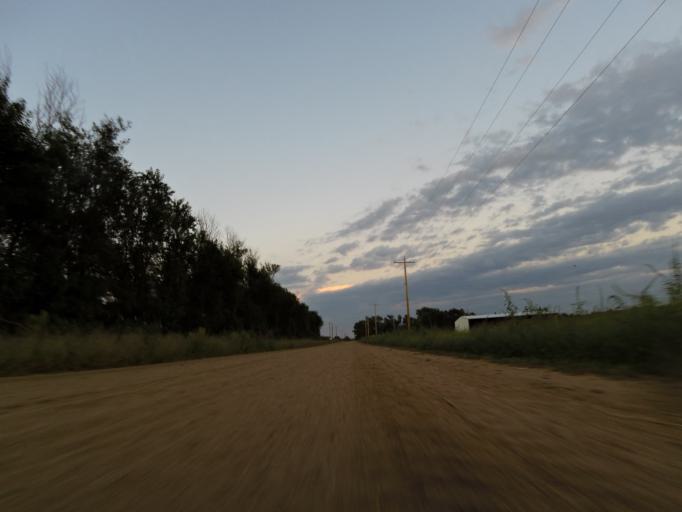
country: US
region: Kansas
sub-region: Reno County
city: South Hutchinson
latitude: 37.9555
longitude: -98.0528
